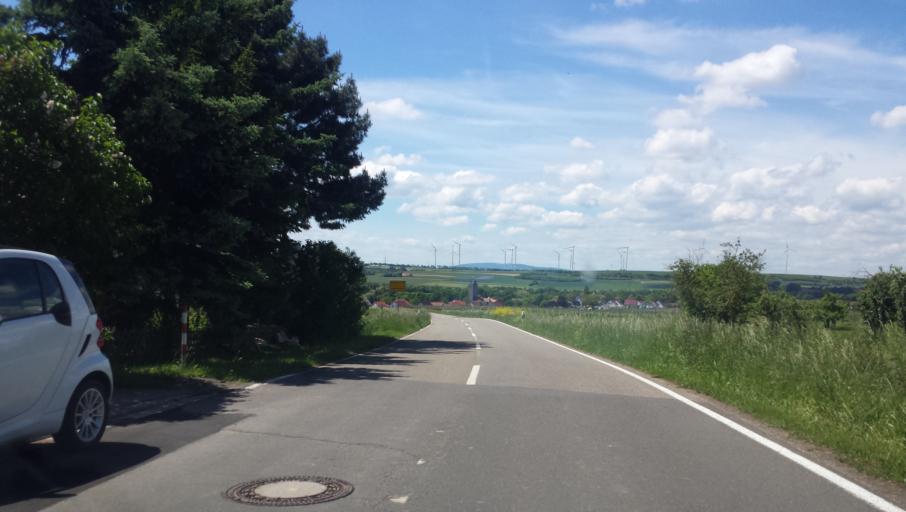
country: DE
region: Rheinland-Pfalz
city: Hangen-Weisheim
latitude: 49.7094
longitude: 8.1805
